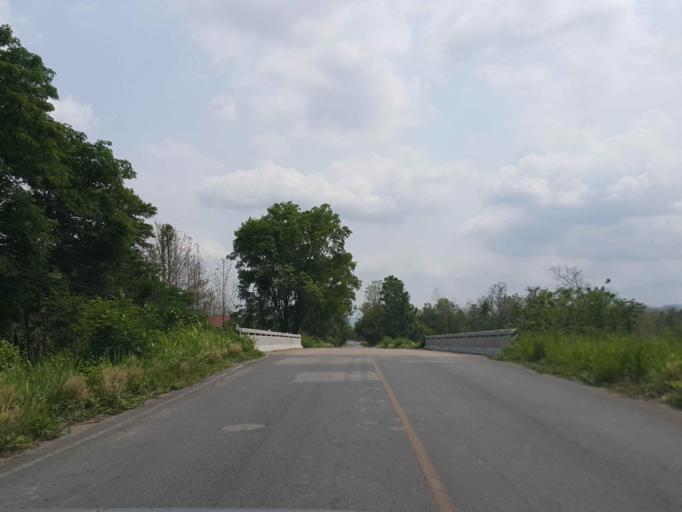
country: TH
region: Lampang
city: Thoen
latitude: 17.5848
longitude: 99.3302
